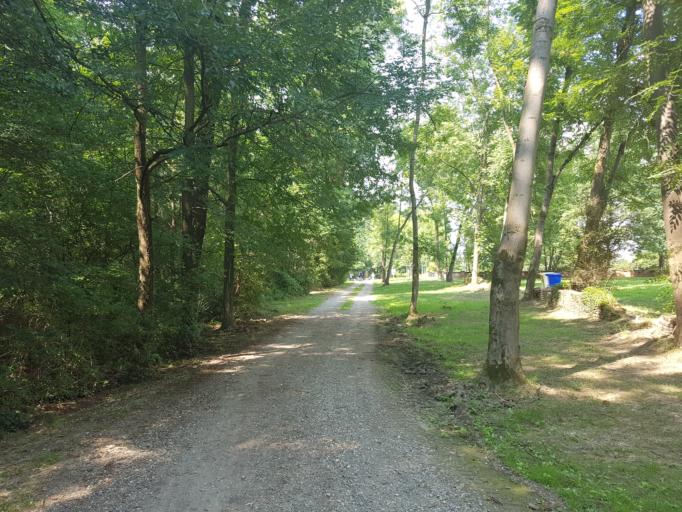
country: IT
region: Piedmont
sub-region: Provincia di Torino
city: Druento
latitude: 45.1475
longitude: 7.5950
